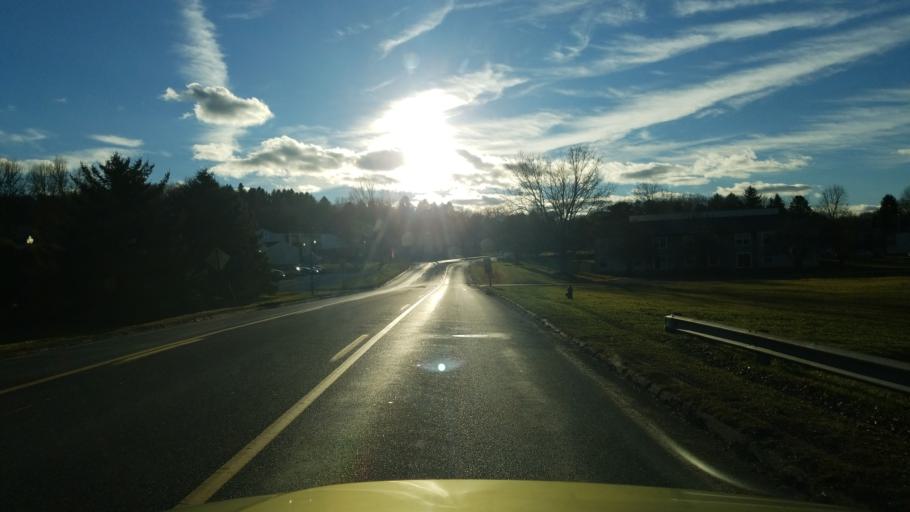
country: US
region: Pennsylvania
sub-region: Indiana County
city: Indiana
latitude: 40.6177
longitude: -79.1902
